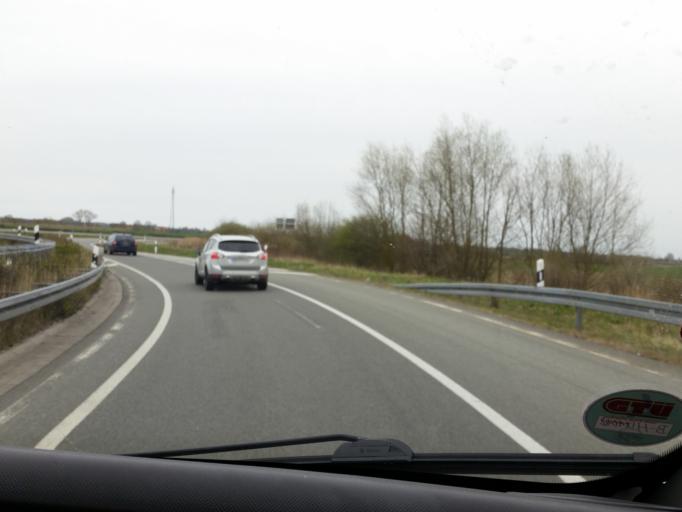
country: DE
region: Mecklenburg-Vorpommern
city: Grimmen
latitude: 54.0837
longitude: 13.1297
